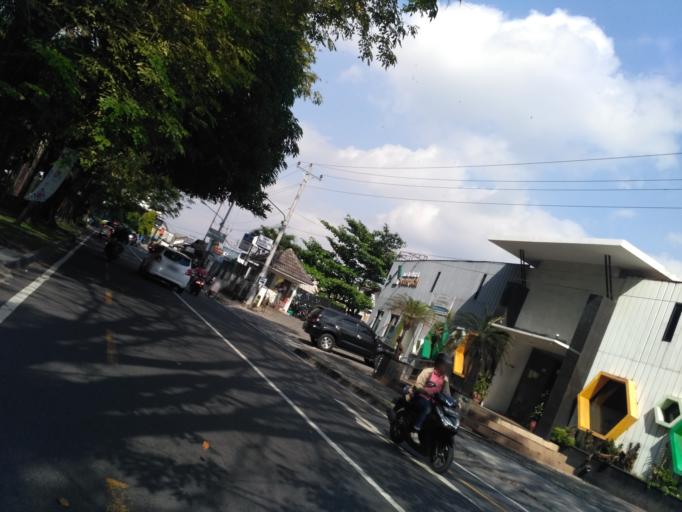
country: ID
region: Daerah Istimewa Yogyakarta
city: Yogyakarta
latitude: -7.7756
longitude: 110.3726
